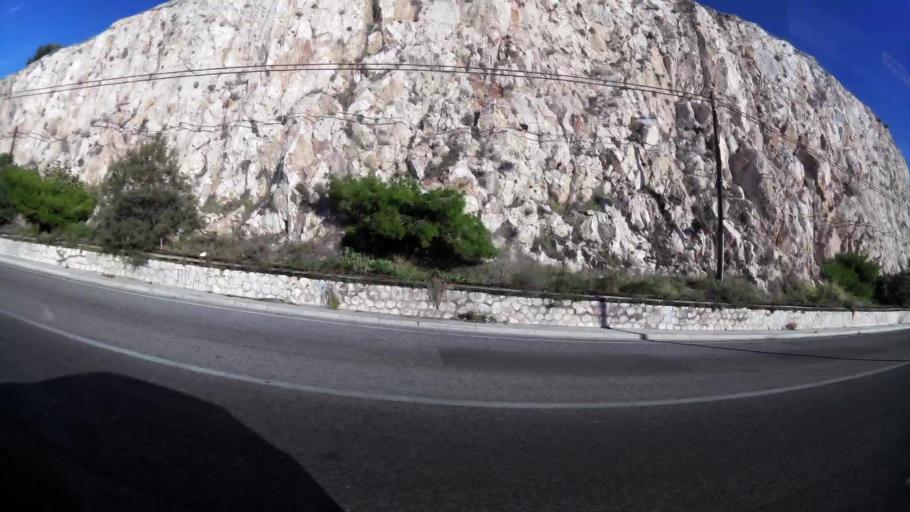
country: GR
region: Attica
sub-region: Nomarchia Athinas
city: Skaramangas
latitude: 38.0165
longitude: 23.5986
